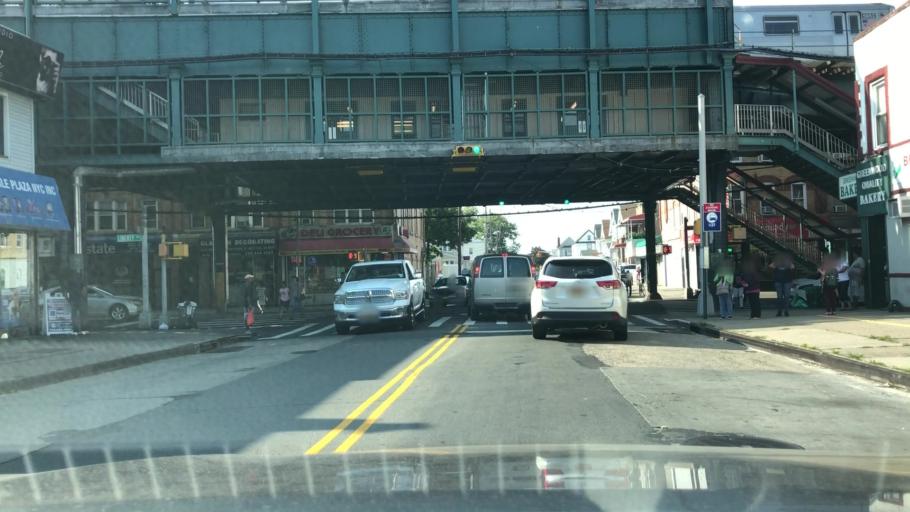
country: US
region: New York
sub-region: Queens County
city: Borough of Queens
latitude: 40.6845
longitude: -73.8310
